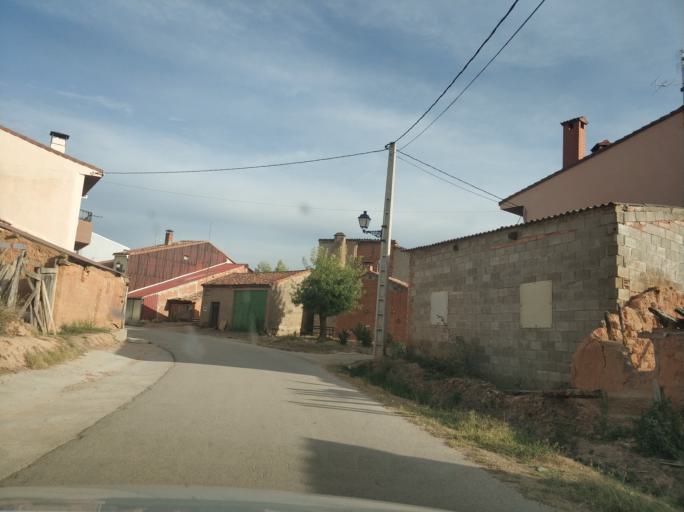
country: ES
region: Castille and Leon
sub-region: Provincia de Soria
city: Fuentearmegil
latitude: 41.6610
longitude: -3.2172
